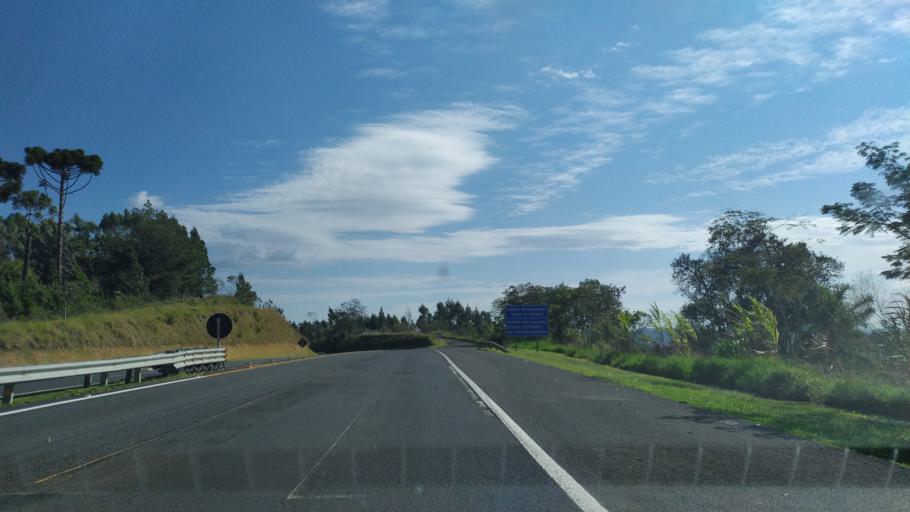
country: BR
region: Parana
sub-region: Telemaco Borba
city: Telemaco Borba
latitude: -24.4190
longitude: -50.7742
